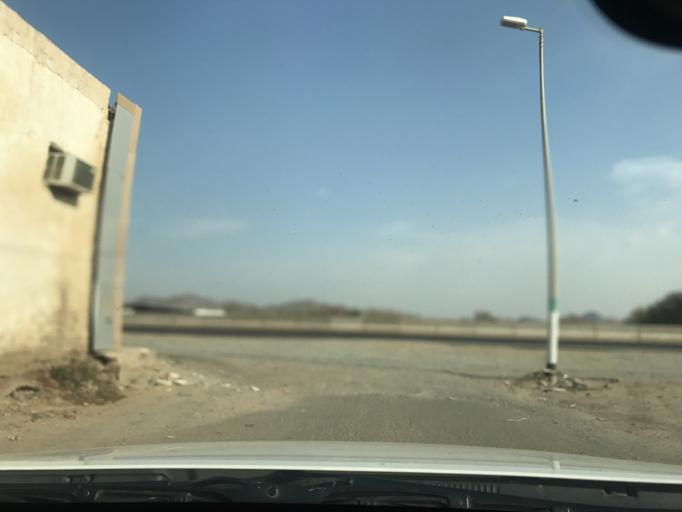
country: SA
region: Makkah
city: Al Jumum
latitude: 21.4419
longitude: 39.5357
